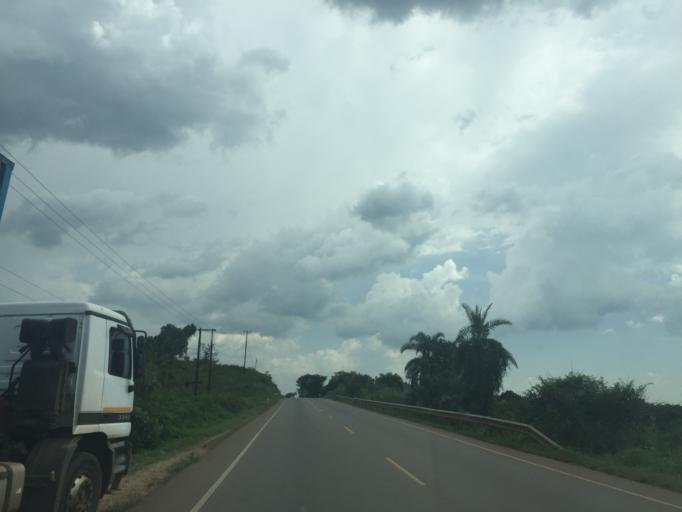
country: UG
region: Central Region
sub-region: Luwero District
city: Wobulenzi
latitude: 0.6631
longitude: 32.5296
